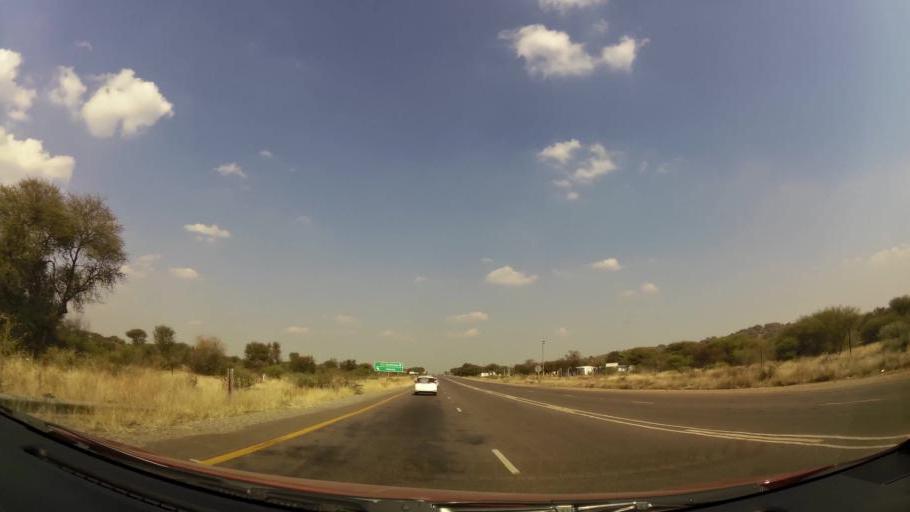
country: ZA
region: North-West
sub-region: Bojanala Platinum District Municipality
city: Mogwase
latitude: -25.4409
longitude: 27.0883
